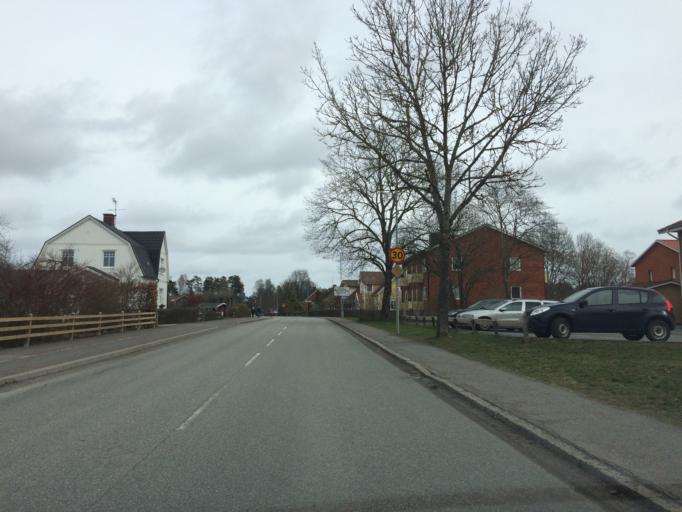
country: SE
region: Skane
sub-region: Osby Kommun
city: Lonsboda
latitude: 56.3986
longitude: 14.3250
